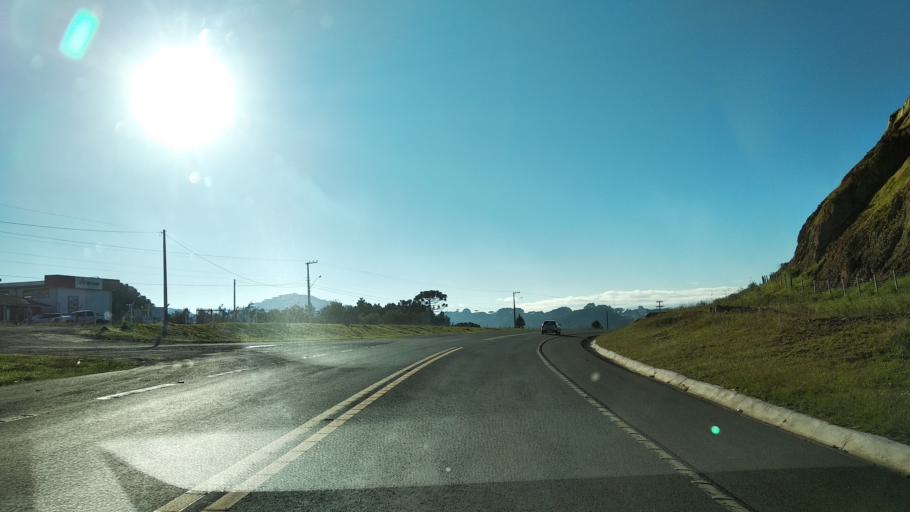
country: BR
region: Santa Catarina
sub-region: Lages
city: Lages
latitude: -27.7926
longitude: -50.3741
